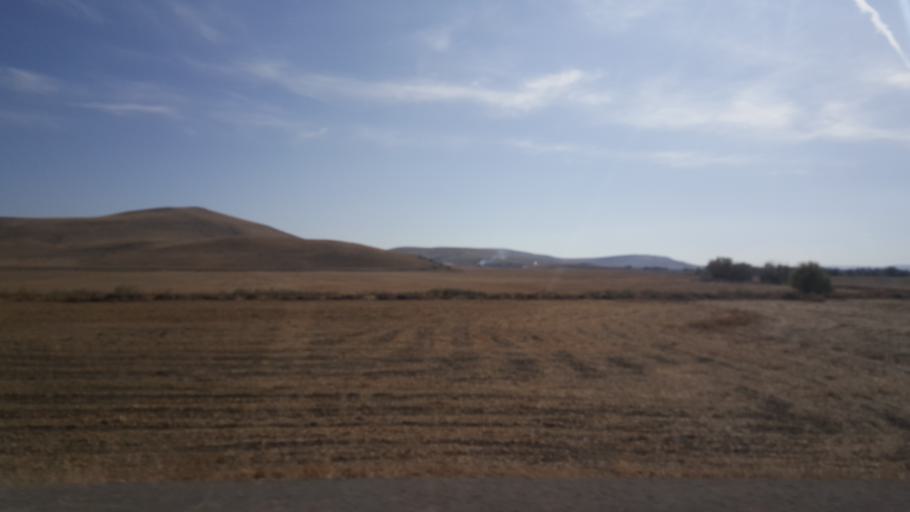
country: TR
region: Ankara
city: Yenice
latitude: 39.3829
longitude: 32.8161
